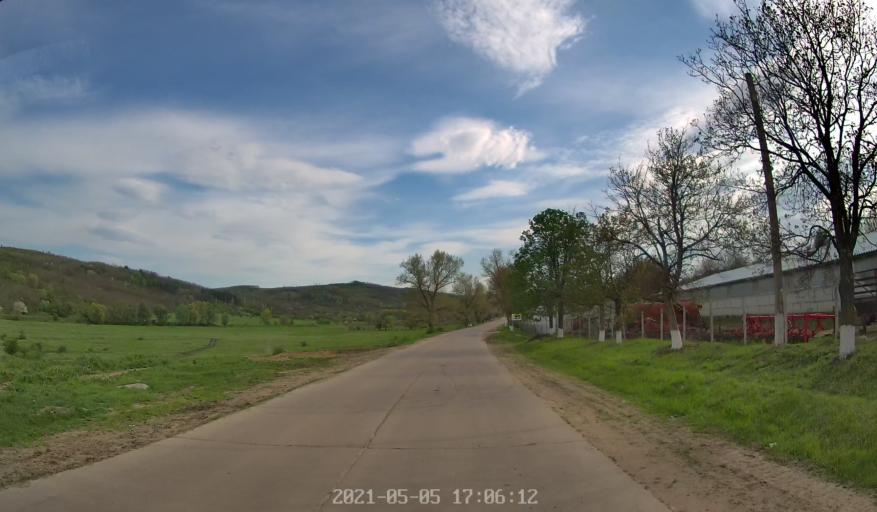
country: MD
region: Chisinau
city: Vadul lui Voda
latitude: 47.0225
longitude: 29.1403
